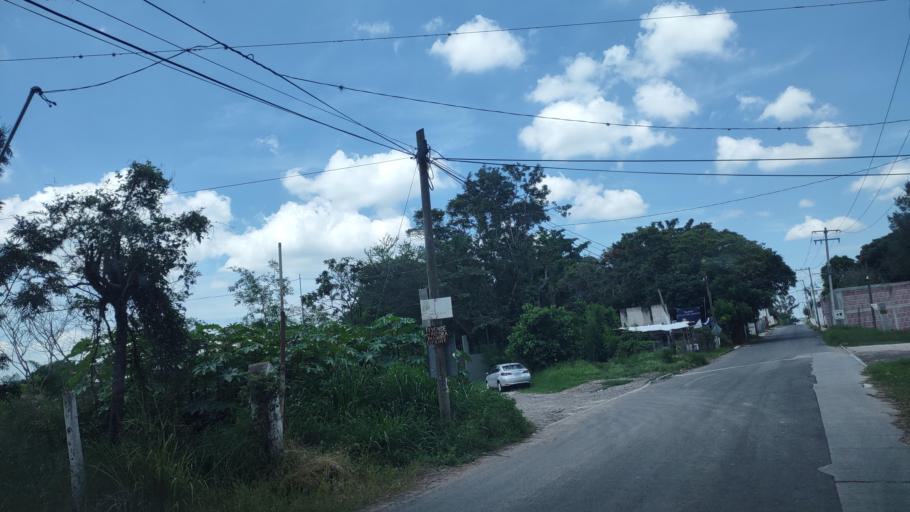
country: MX
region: Veracruz
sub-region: Emiliano Zapata
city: Dos Rios
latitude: 19.4937
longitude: -96.8102
